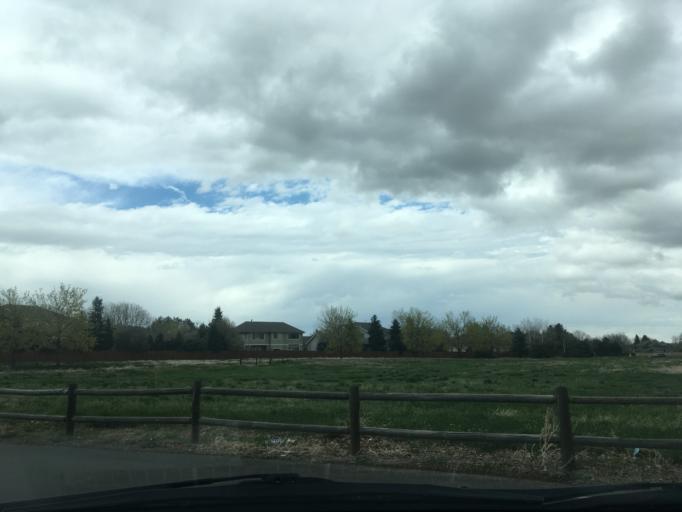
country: US
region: Colorado
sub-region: Boulder County
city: Louisville
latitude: 40.0160
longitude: -105.1302
